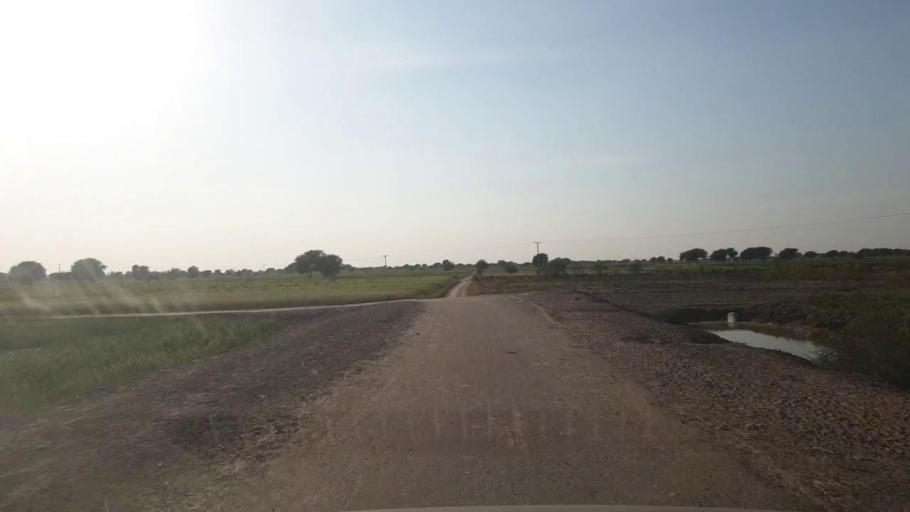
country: PK
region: Sindh
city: Chambar
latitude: 25.2798
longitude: 68.7482
